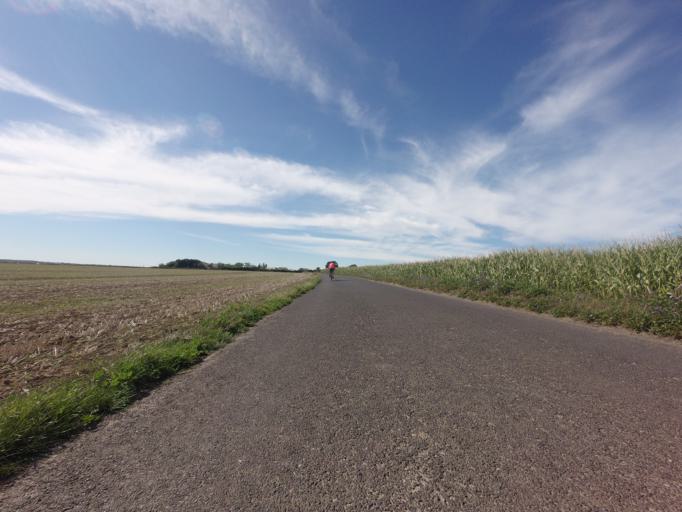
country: GB
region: England
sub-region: Kent
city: Birchington-on-Sea
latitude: 51.3478
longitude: 1.2592
